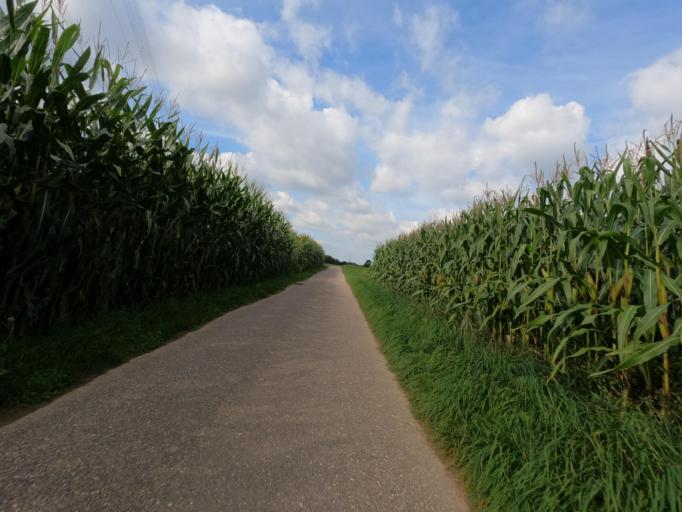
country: DE
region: North Rhine-Westphalia
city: Geilenkirchen
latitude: 50.9682
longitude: 6.1492
